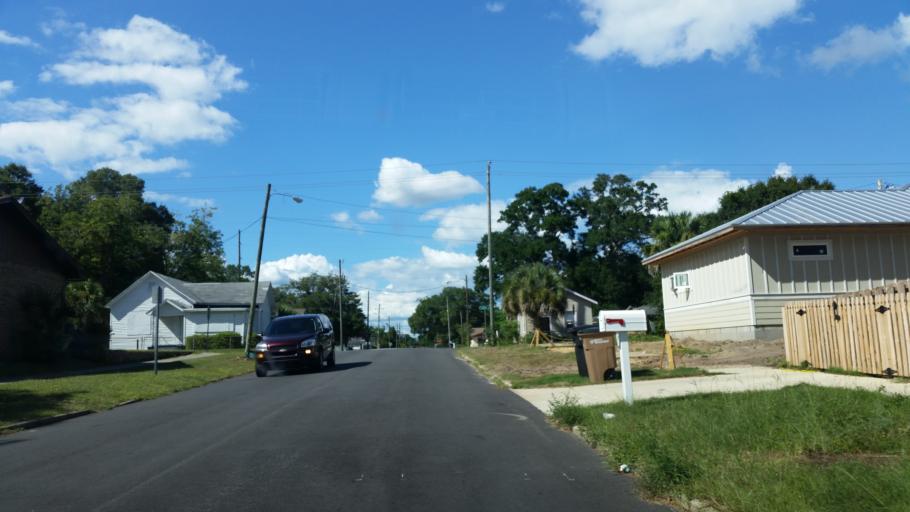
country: US
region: Florida
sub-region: Escambia County
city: Pensacola
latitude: 30.4168
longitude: -87.2303
